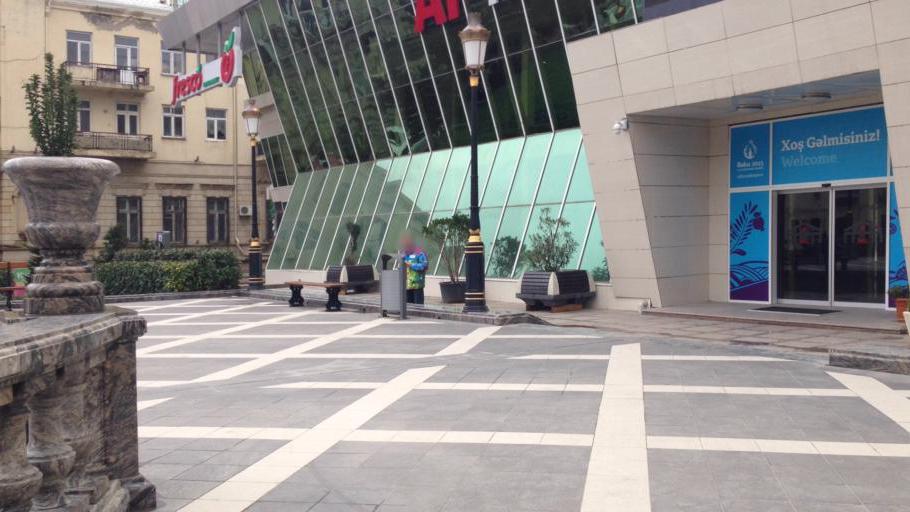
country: AZ
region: Baki
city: Baku
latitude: 40.3767
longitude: 49.8422
